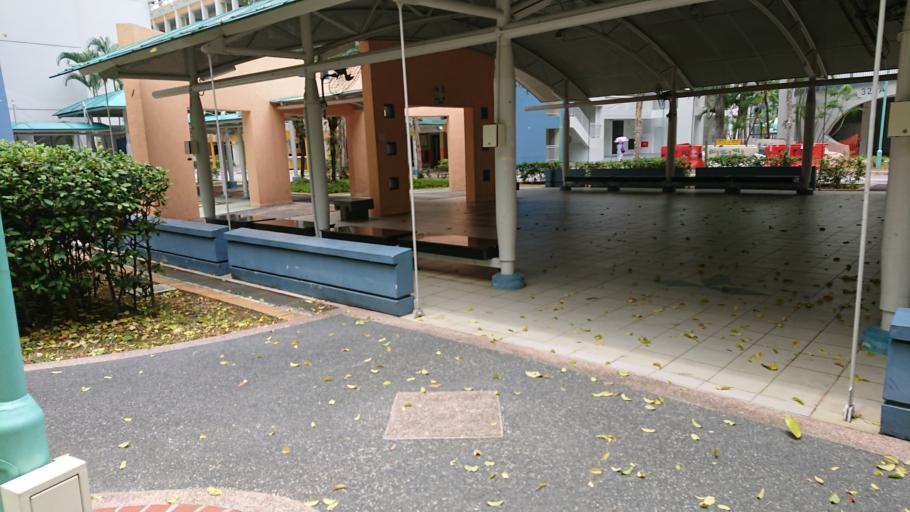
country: MY
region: Johor
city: Kampung Pasir Gudang Baru
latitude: 1.3907
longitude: 103.8911
